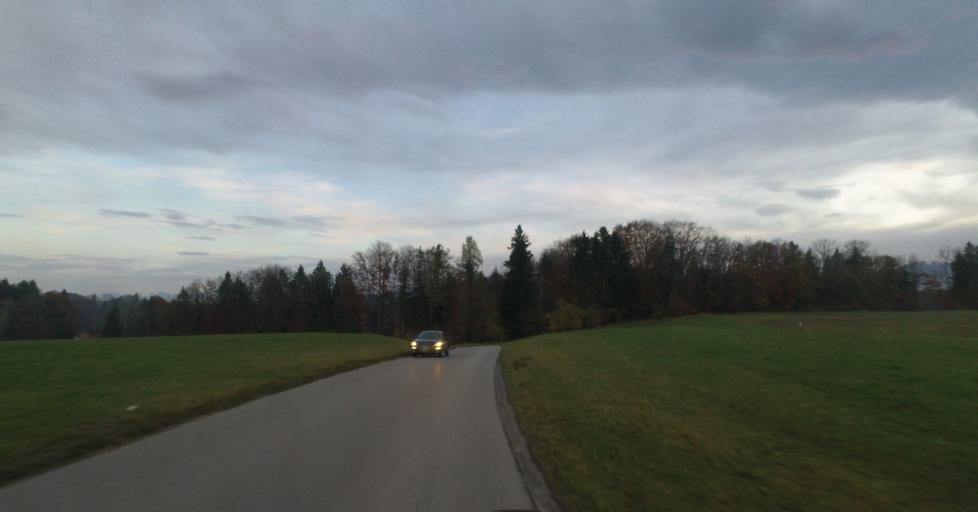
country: DE
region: Bavaria
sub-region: Upper Bavaria
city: Prien am Chiemsee
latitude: 47.8417
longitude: 12.3168
